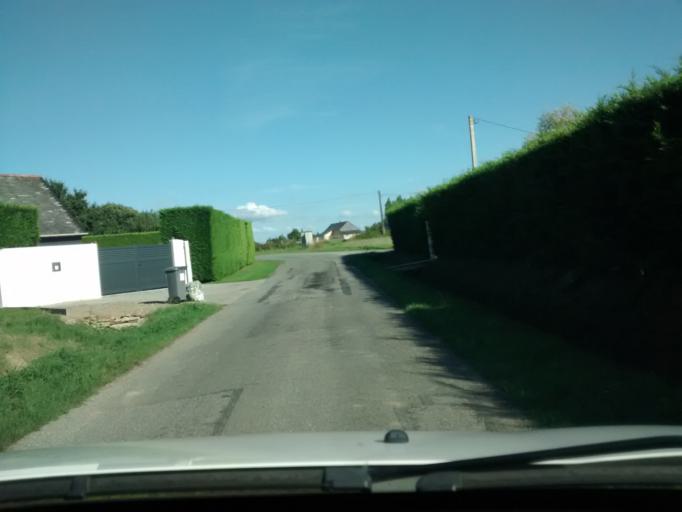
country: FR
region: Brittany
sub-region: Departement d'Ille-et-Vilaine
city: Nouvoitou
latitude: 48.0761
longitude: -1.5484
